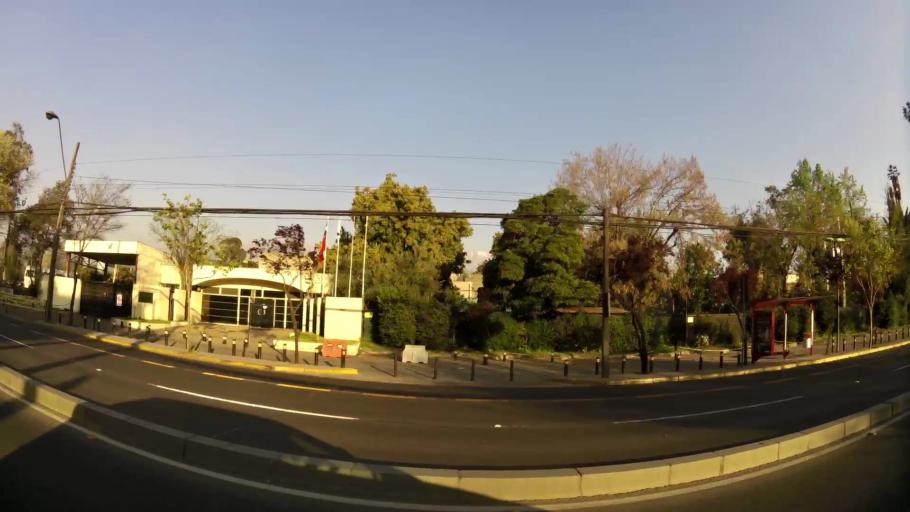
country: CL
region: Santiago Metropolitan
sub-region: Provincia de Santiago
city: Villa Presidente Frei, Nunoa, Santiago, Chile
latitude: -33.3964
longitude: -70.5498
